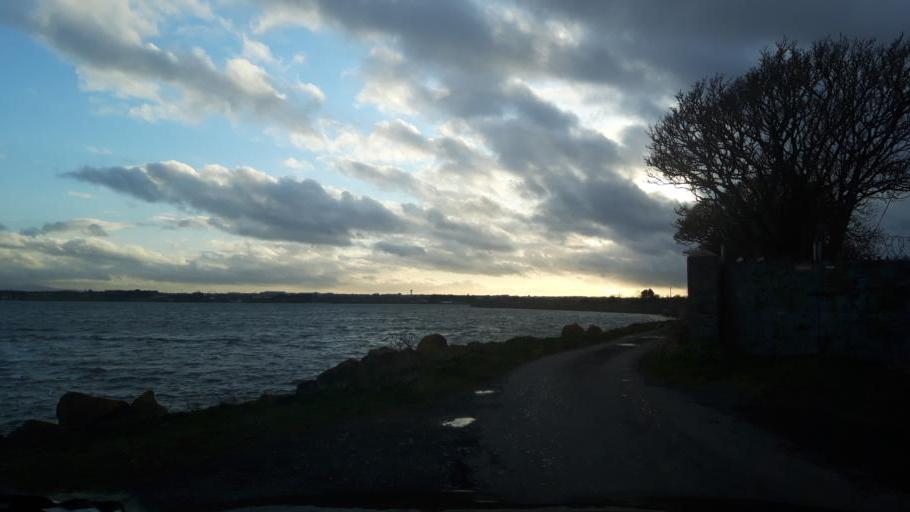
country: IE
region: Leinster
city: Malahide
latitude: 53.4696
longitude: -6.1726
